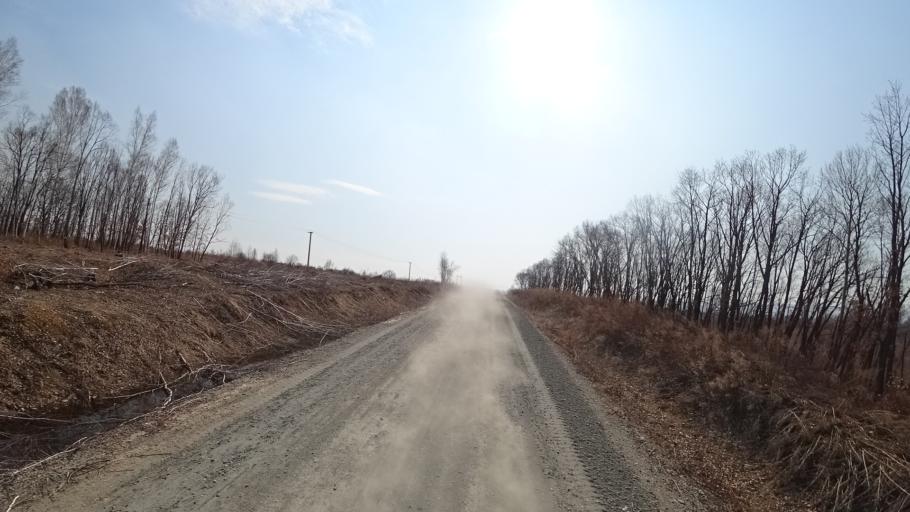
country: RU
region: Amur
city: Novobureyskiy
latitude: 49.8196
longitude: 129.9808
